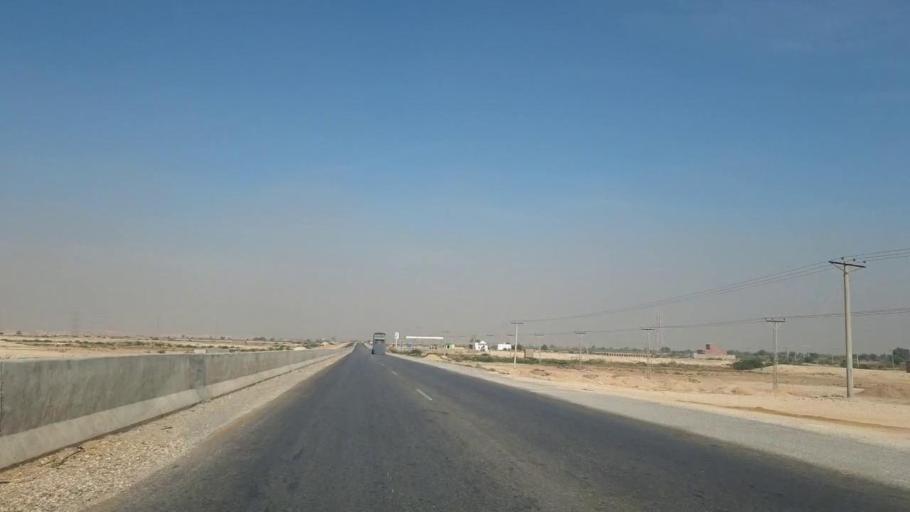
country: PK
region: Sindh
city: Jamshoro
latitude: 25.5102
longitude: 68.2735
